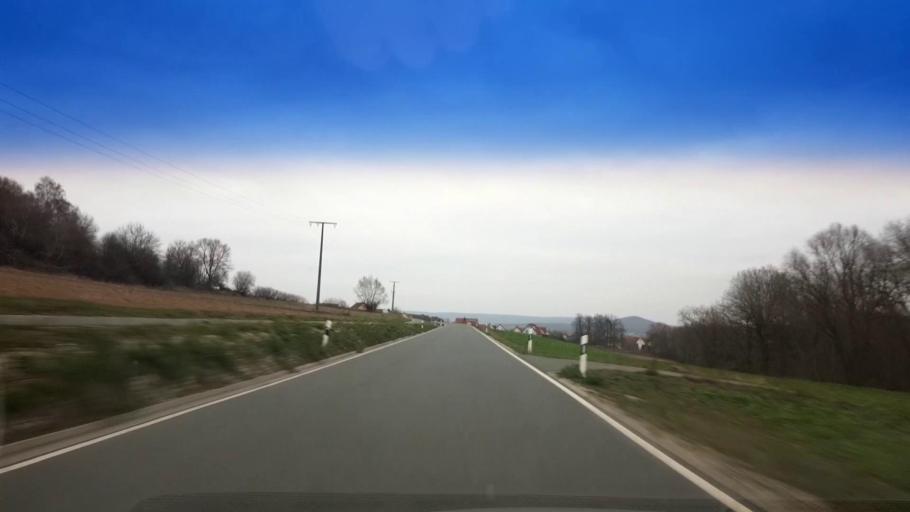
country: DE
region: Bavaria
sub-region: Upper Franconia
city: Hallerndorf
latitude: 49.7692
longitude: 10.9952
